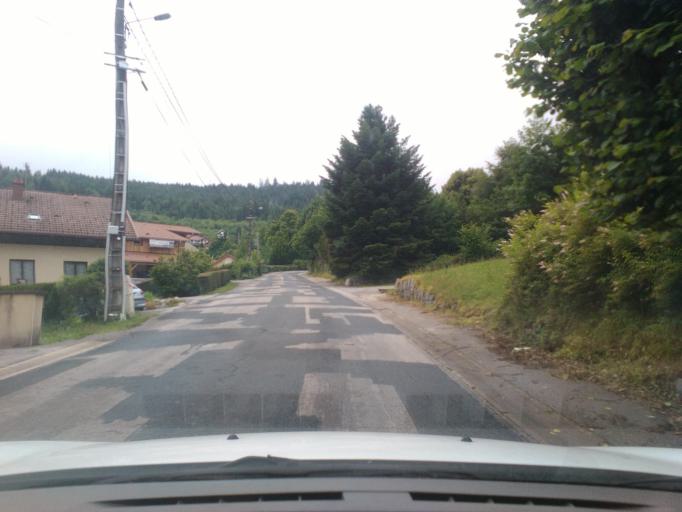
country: FR
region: Lorraine
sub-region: Departement des Vosges
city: Gerardmer
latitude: 48.0751
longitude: 6.8626
